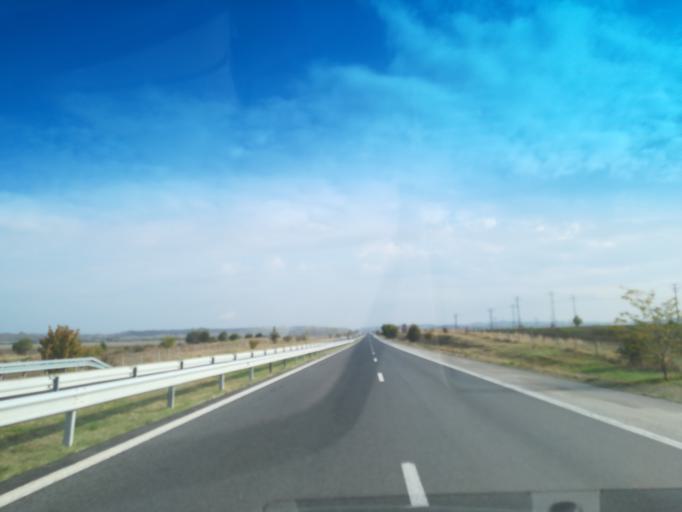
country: BG
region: Stara Zagora
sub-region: Obshtina Chirpan
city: Chirpan
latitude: 42.2116
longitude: 25.3122
